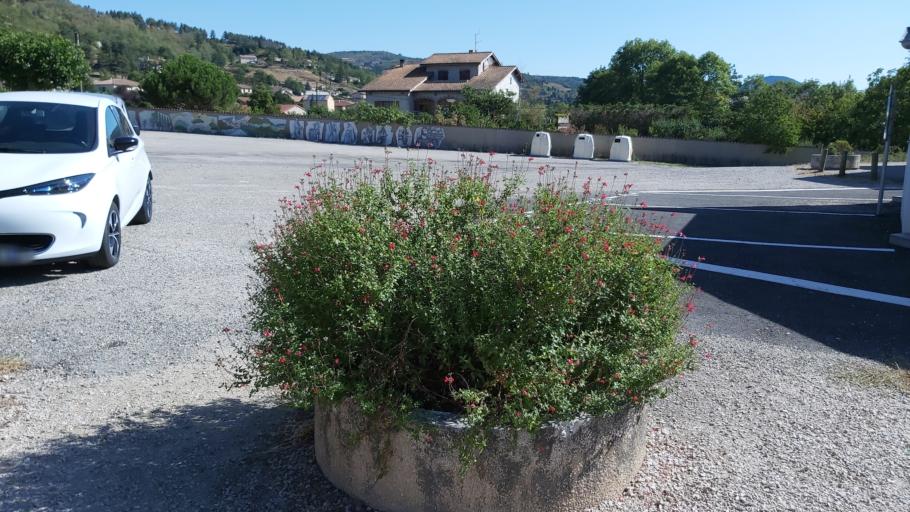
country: FR
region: Rhone-Alpes
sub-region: Departement de l'Ardeche
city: Villevocance
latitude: 45.2292
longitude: 4.5949
